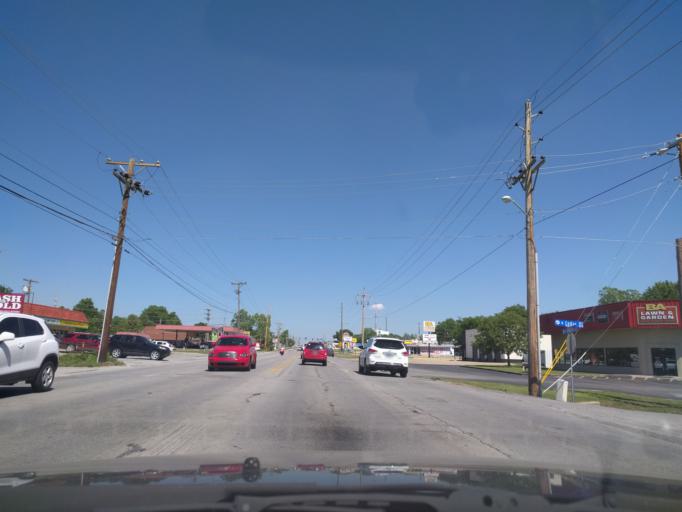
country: US
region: Oklahoma
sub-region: Tulsa County
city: Broken Arrow
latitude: 36.0609
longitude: -95.7947
